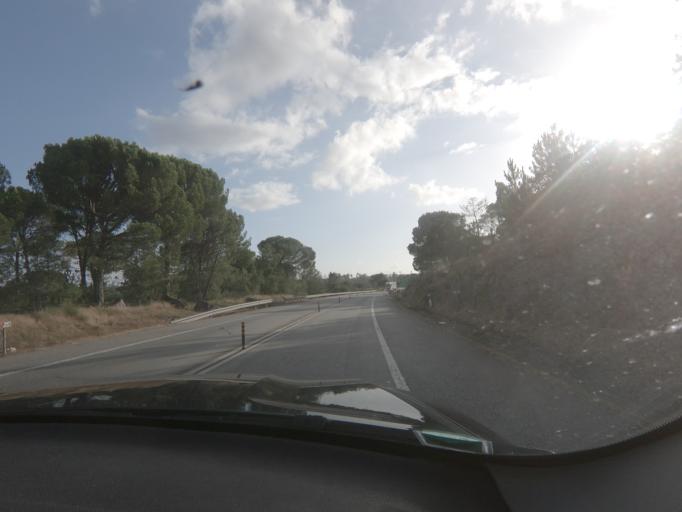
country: PT
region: Viseu
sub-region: Concelho de Tondela
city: Tondela
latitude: 40.5291
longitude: -8.0683
